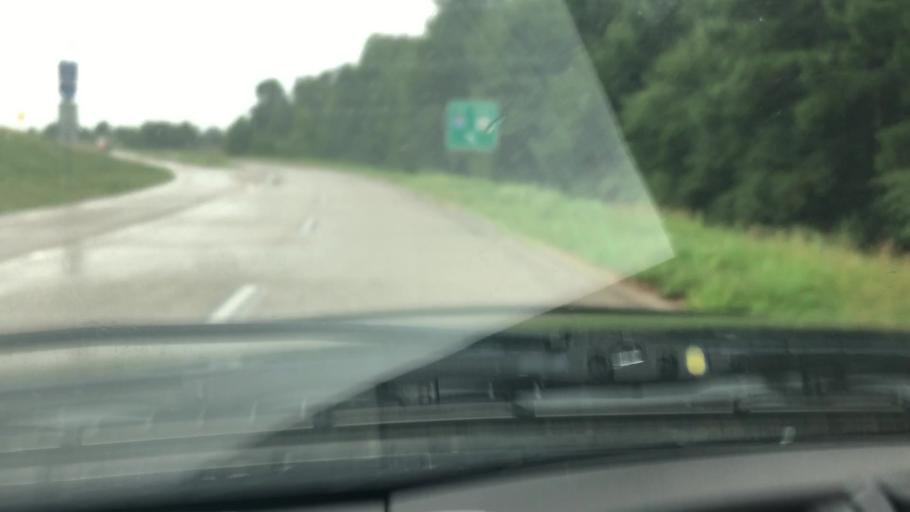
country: US
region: Texas
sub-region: Bowie County
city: Wake Village
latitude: 33.3909
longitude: -94.0982
